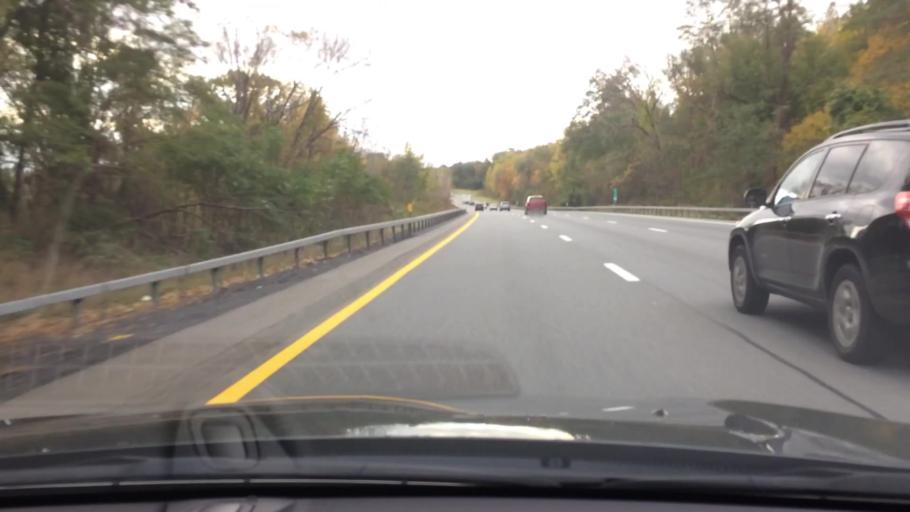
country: US
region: New York
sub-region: Saratoga County
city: Country Knolls
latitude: 42.9211
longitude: -73.8008
